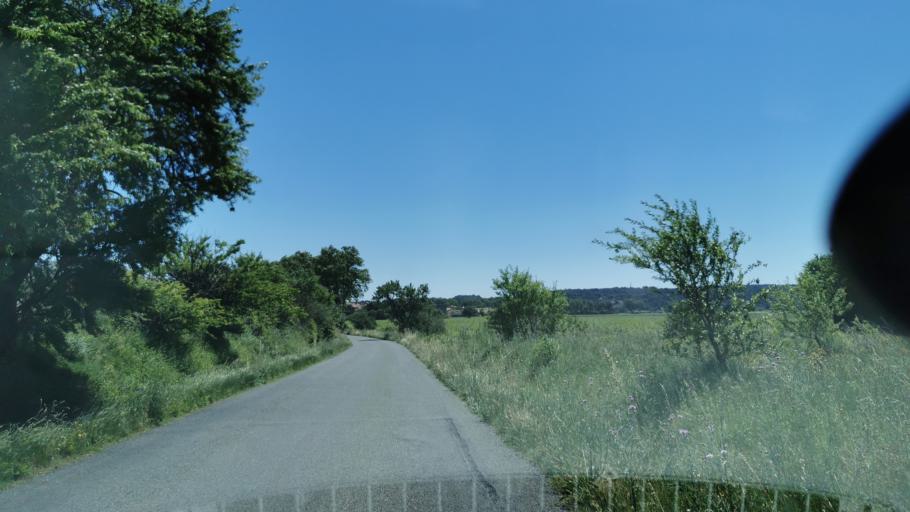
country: FR
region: Languedoc-Roussillon
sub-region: Departement de l'Aude
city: Marcorignan
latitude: 43.2433
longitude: 2.9147
